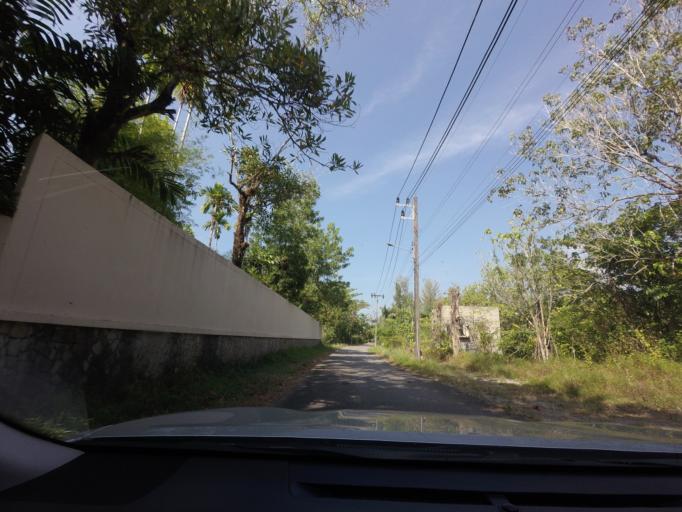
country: TH
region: Phangnga
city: Ban Khao Lak
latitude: 8.7355
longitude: 98.2428
